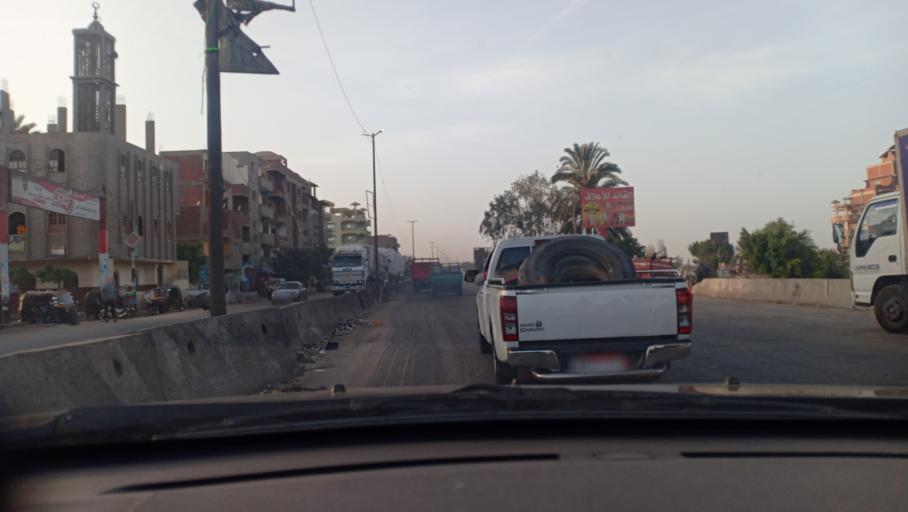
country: EG
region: Muhafazat al Minufiyah
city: Quwaysina
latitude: 30.5776
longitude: 31.2735
